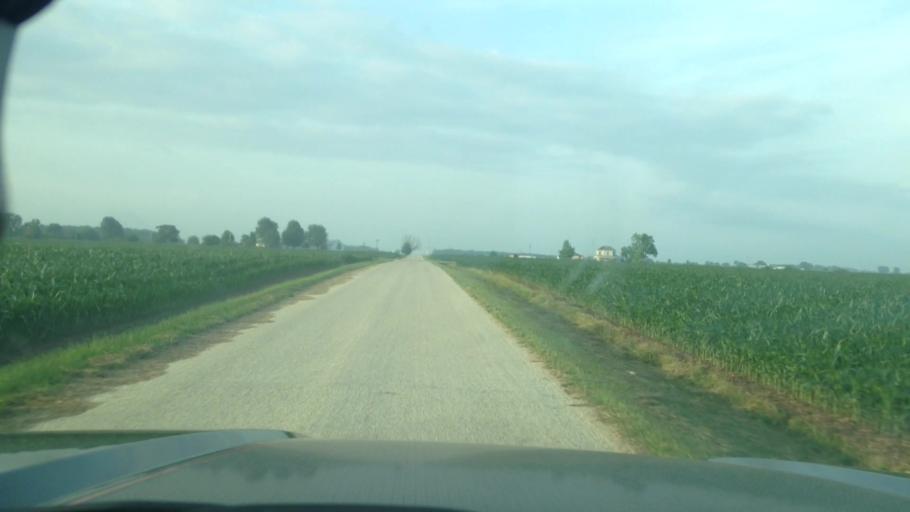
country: US
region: Indiana
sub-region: Randolph County
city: Union City
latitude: 40.2382
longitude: -84.8626
